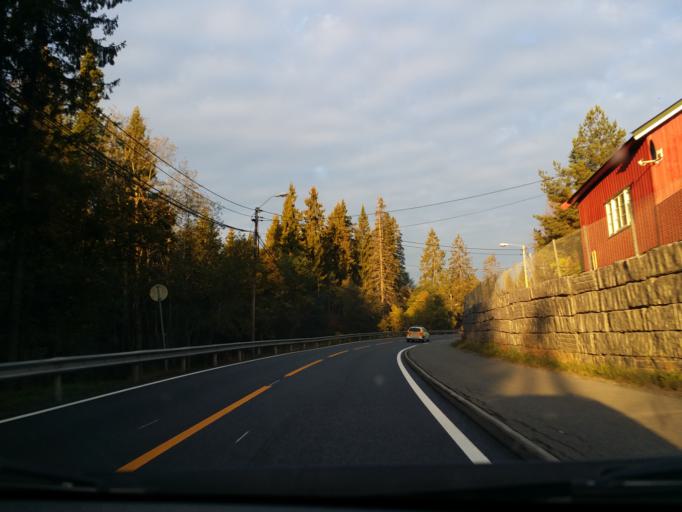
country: NO
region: Akershus
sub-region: Baerum
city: Skui
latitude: 59.9585
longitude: 10.3640
